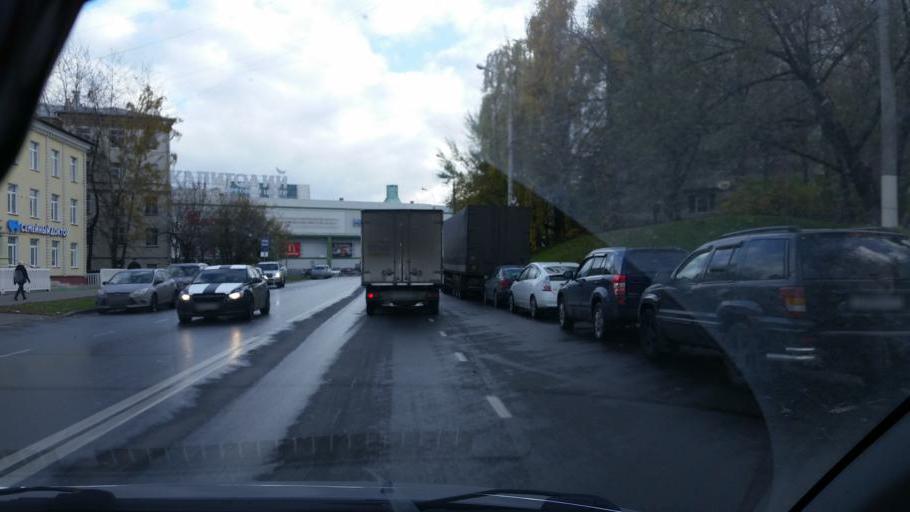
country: RU
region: Moscow
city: Novyye Cheremushki
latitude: 55.6883
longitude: 37.6015
